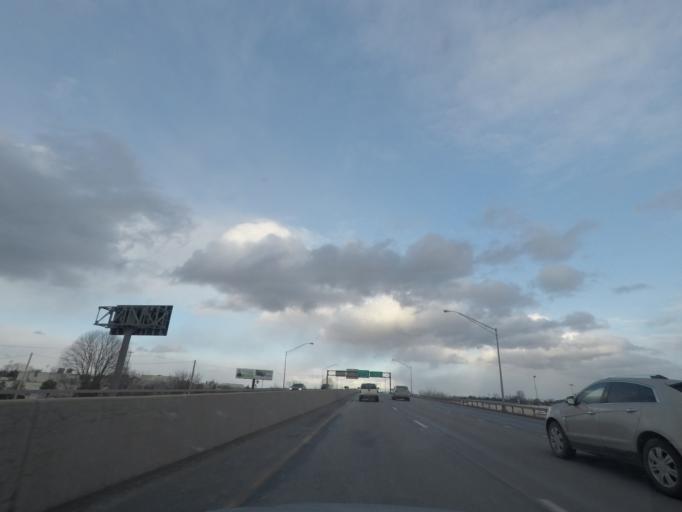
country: US
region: New York
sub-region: Oneida County
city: New Hartford
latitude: 43.0843
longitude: -75.2862
